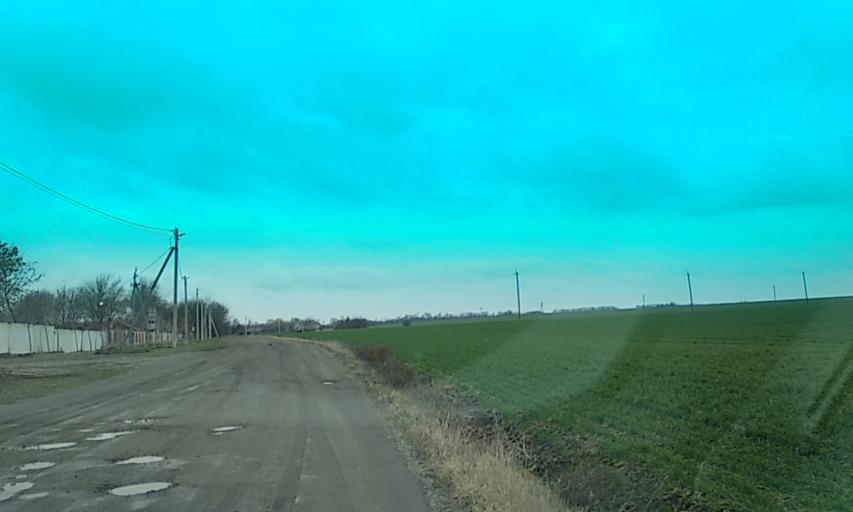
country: RU
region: Krasnodarskiy
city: Vyselki
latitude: 45.6615
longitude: 39.7035
